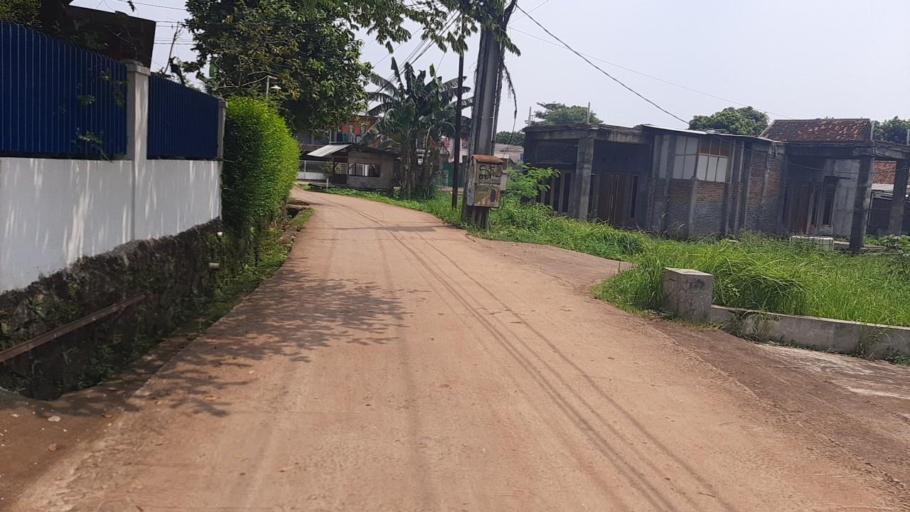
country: ID
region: West Java
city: Cileungsir
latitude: -6.4224
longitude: 106.9134
